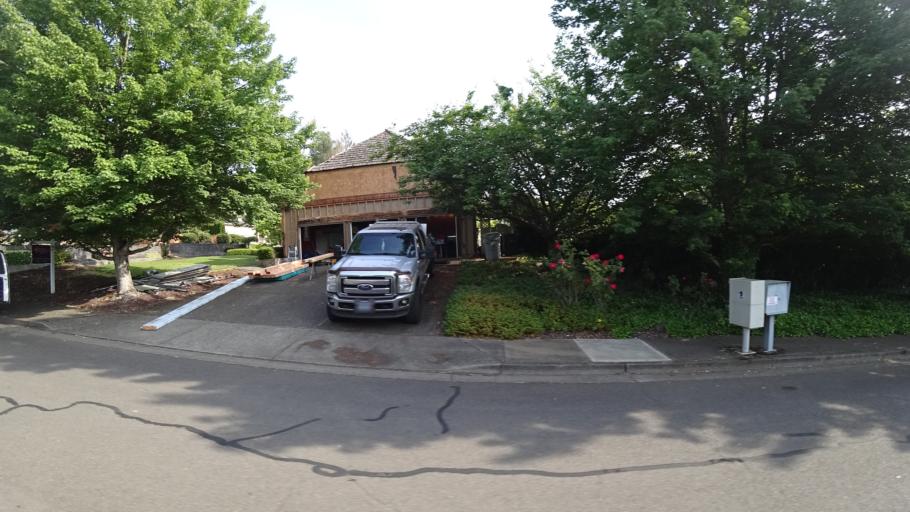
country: US
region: Oregon
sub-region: Clackamas County
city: Happy Valley
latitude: 45.4486
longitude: -122.5292
